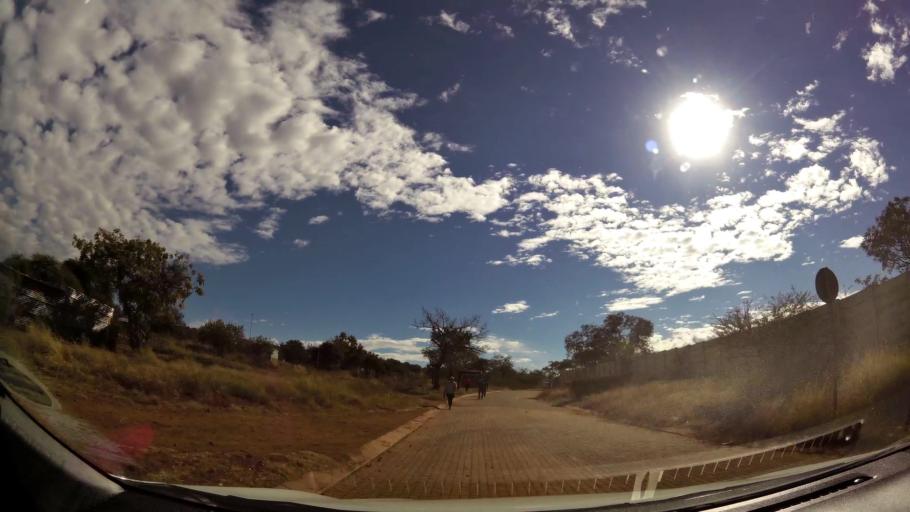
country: ZA
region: Limpopo
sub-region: Waterberg District Municipality
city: Warmbaths
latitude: -24.8756
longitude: 28.2734
